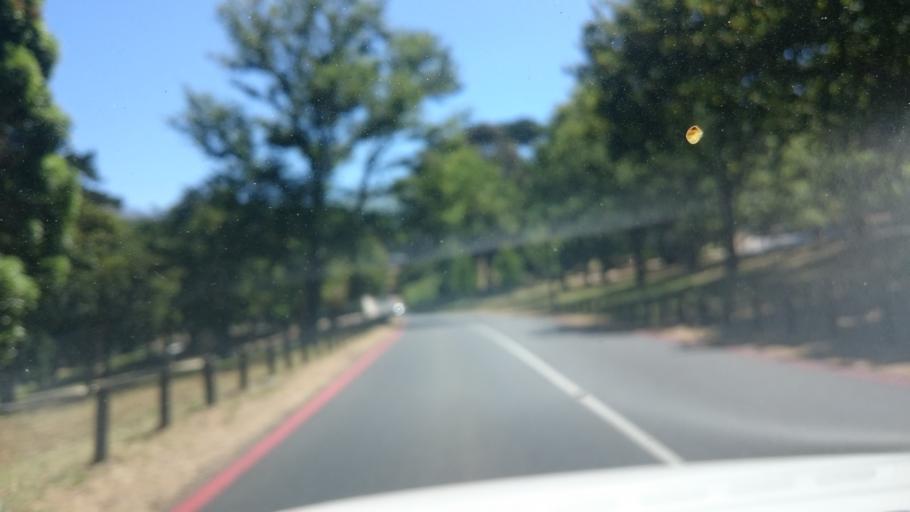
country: ZA
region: Western Cape
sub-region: City of Cape Town
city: Newlands
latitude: -33.9993
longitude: 18.4522
